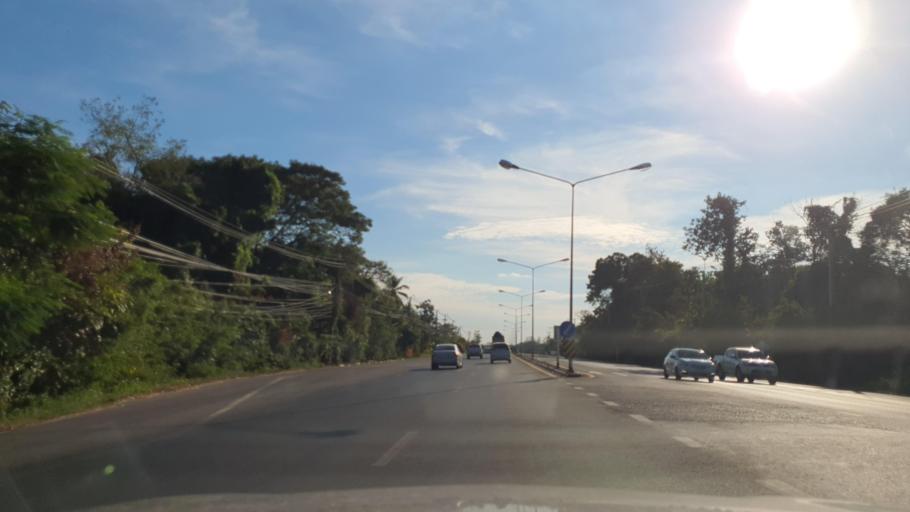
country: TH
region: Kalasin
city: Yang Talat
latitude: 16.3690
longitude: 103.3440
